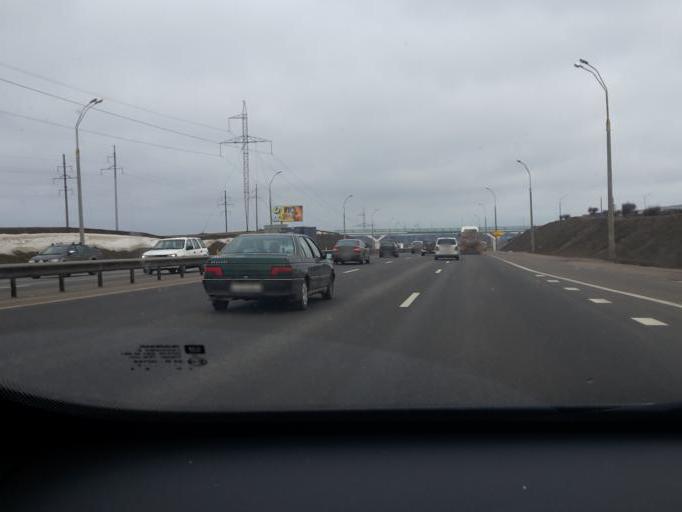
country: BY
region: Minsk
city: Malinovka
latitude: 53.8831
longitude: 27.4163
